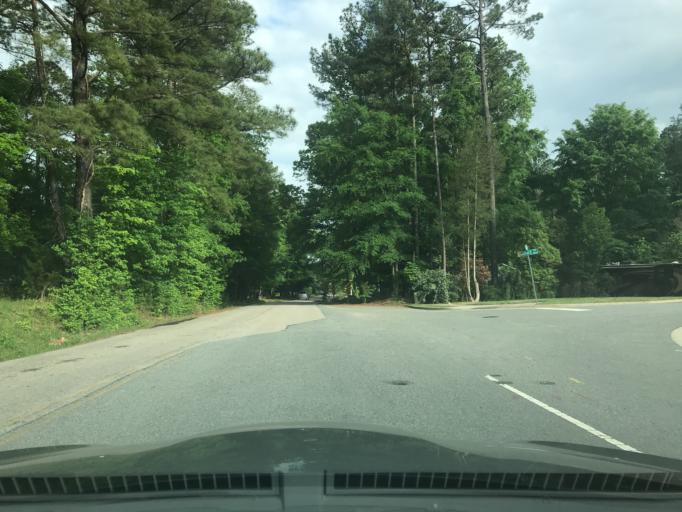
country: US
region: North Carolina
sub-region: Wake County
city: Wake Forest
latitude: 35.9235
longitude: -78.5744
